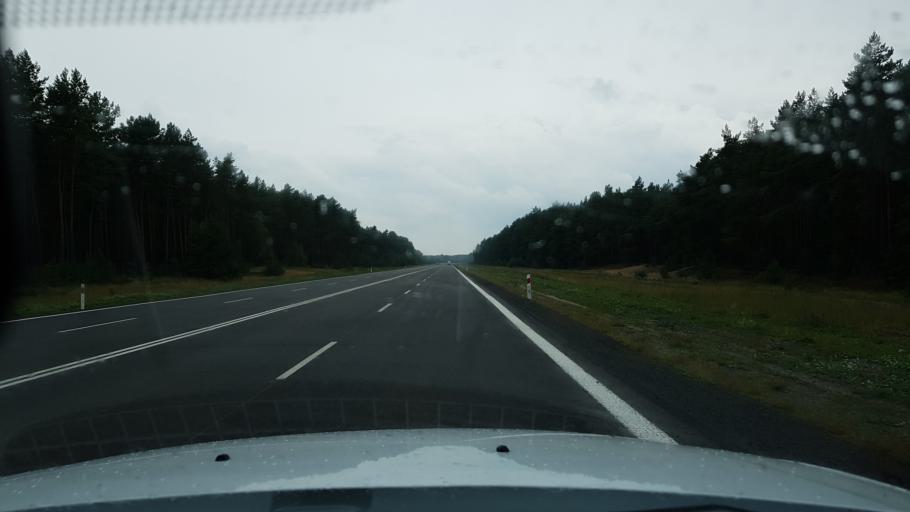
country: PL
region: West Pomeranian Voivodeship
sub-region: Powiat stargardzki
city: Kobylanka
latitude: 53.4275
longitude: 14.8053
